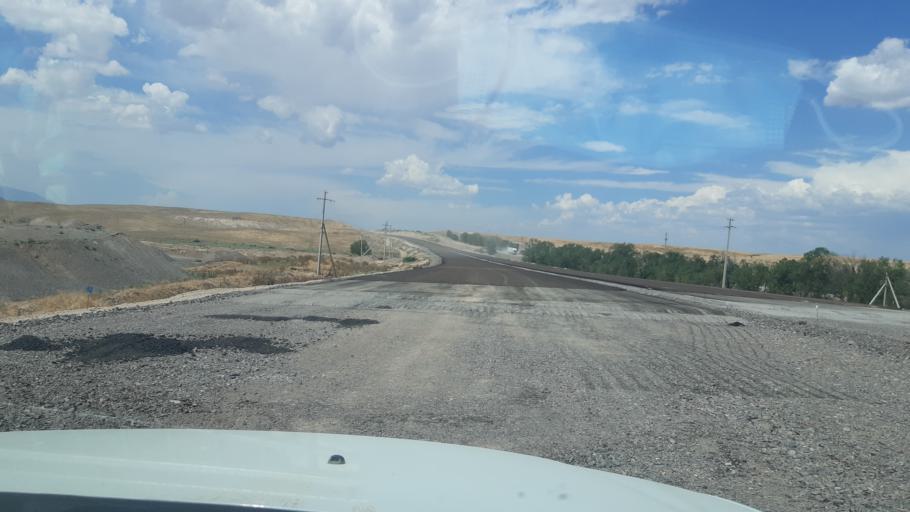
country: KG
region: Chuy
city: Bystrovka
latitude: 43.3205
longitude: 76.0642
